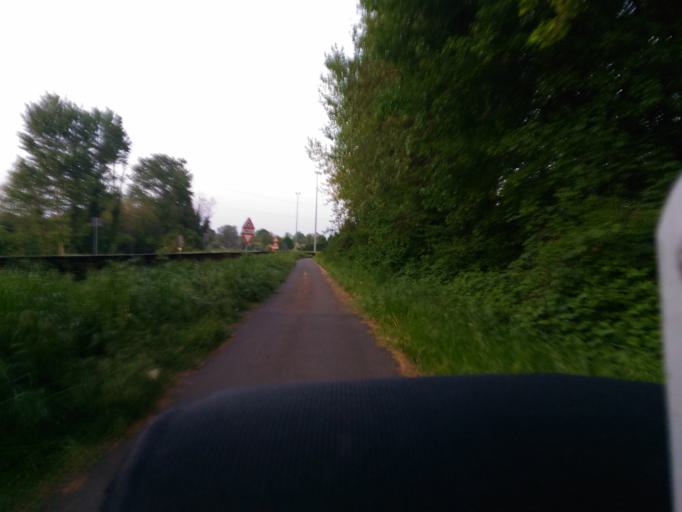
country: IT
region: Lombardy
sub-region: Provincia di Lodi
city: Muzza di Cornegliano Laudense
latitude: 45.3079
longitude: 9.4691
